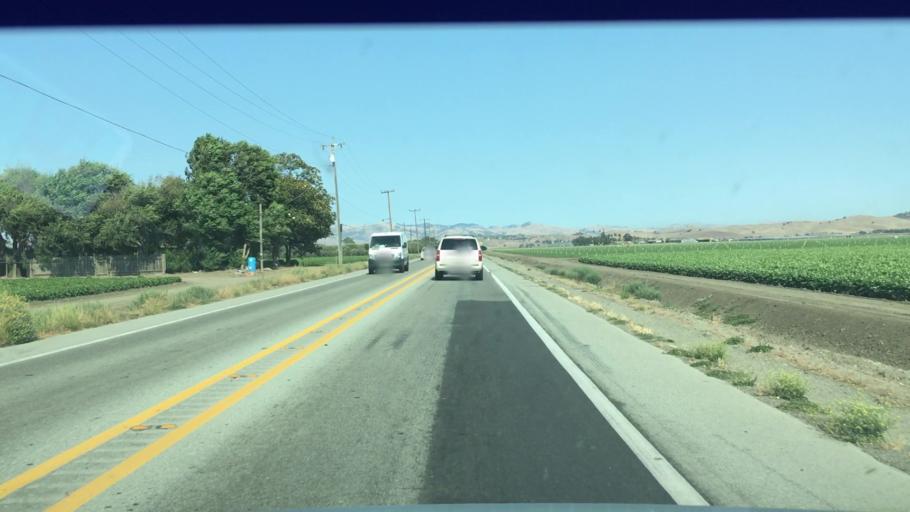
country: US
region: California
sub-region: San Benito County
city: San Juan Bautista
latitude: 36.8411
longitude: -121.5136
